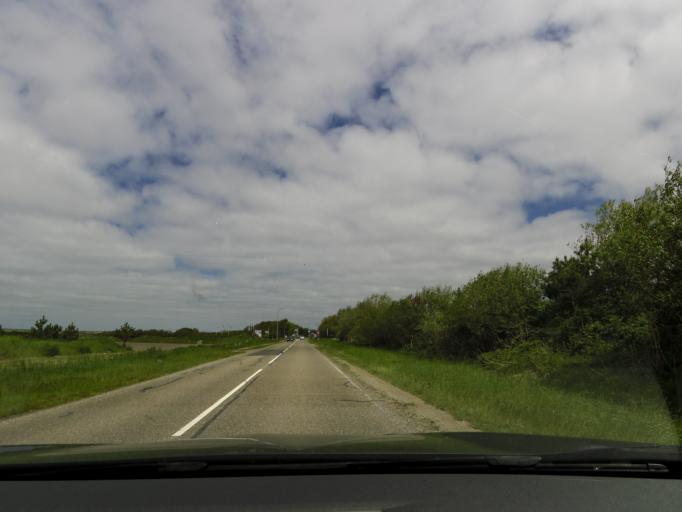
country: NL
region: South Holland
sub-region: Gemeente Goeree-Overflakkee
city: Ouddorp
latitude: 51.8191
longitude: 3.9044
